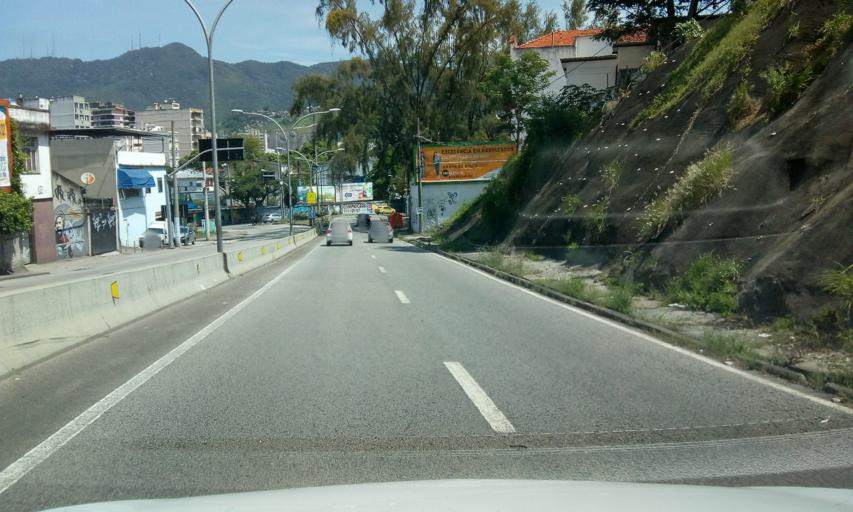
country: BR
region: Rio de Janeiro
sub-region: Rio De Janeiro
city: Rio de Janeiro
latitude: -22.9161
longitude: -43.2634
